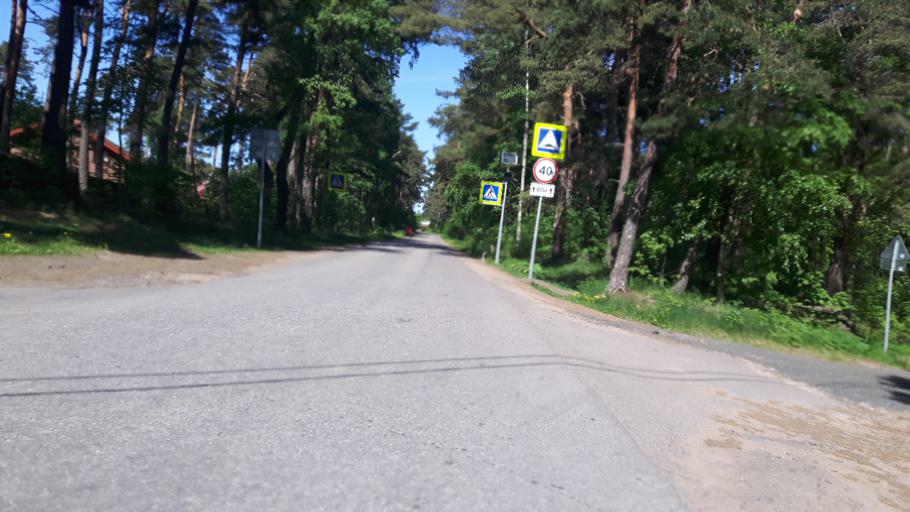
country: RU
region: Leningrad
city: Lebyazh'ye
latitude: 59.9644
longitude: 29.4087
